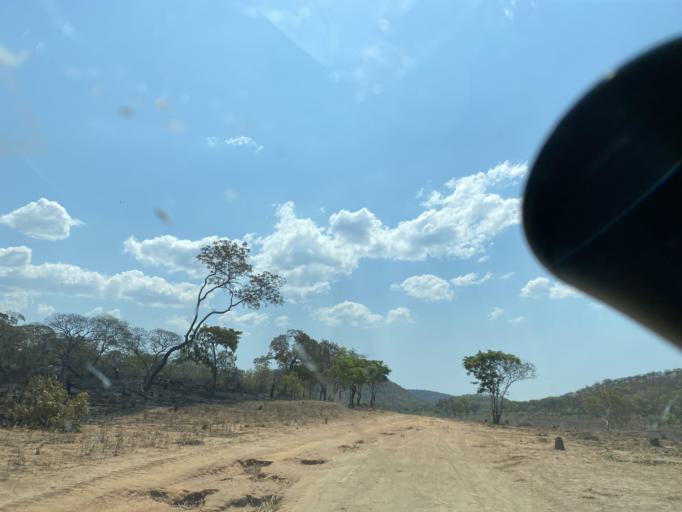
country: ZM
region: Lusaka
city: Chongwe
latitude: -15.0842
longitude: 29.4791
